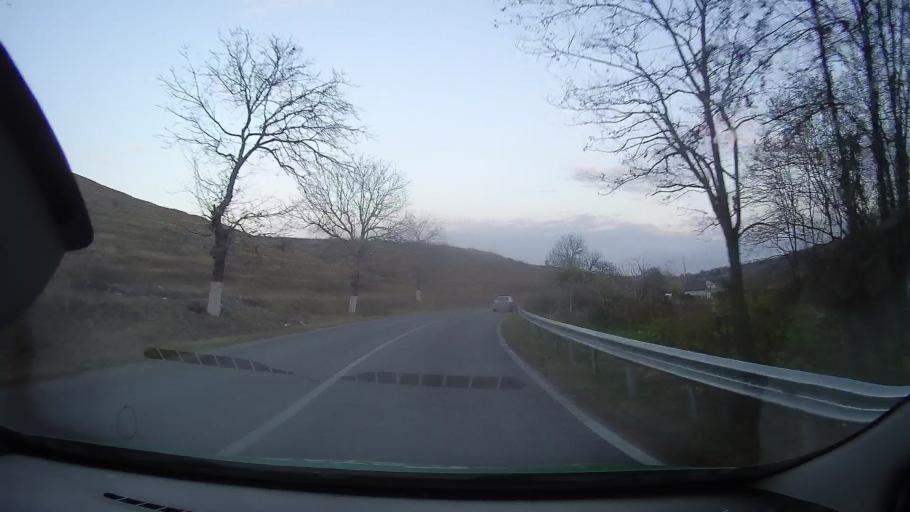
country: RO
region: Constanta
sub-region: Comuna Baneasa
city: Baneasa
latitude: 44.0768
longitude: 27.6751
